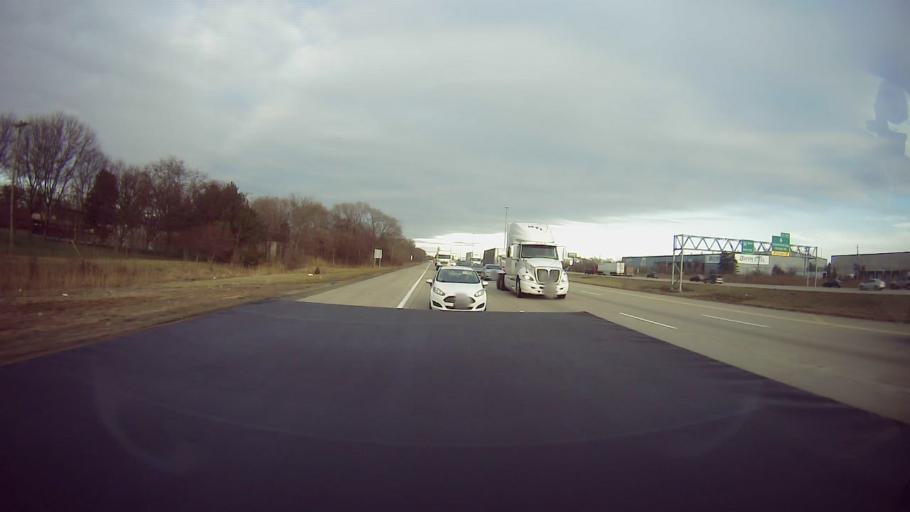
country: US
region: Michigan
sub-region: Wayne County
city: Allen Park
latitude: 42.2662
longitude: -83.2419
